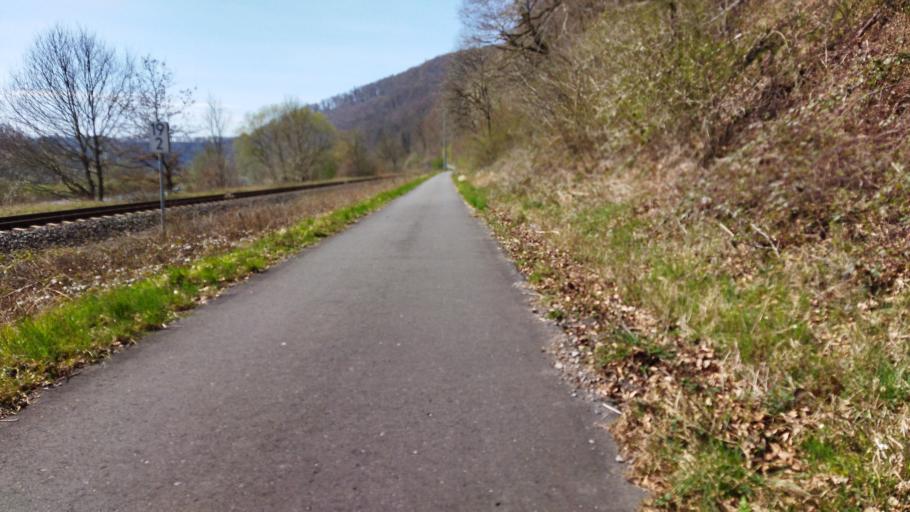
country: DE
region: Lower Saxony
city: Bad Karlshafen
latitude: 51.6557
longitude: 9.4714
